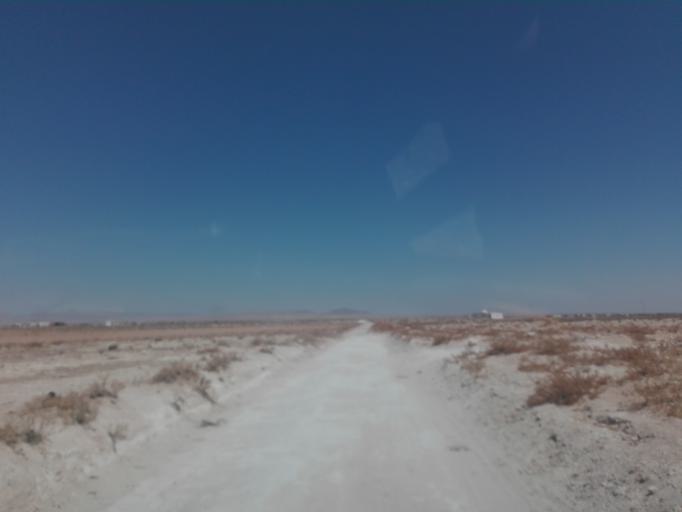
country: TN
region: Safaqis
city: Skhira
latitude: 34.3809
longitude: 9.9259
